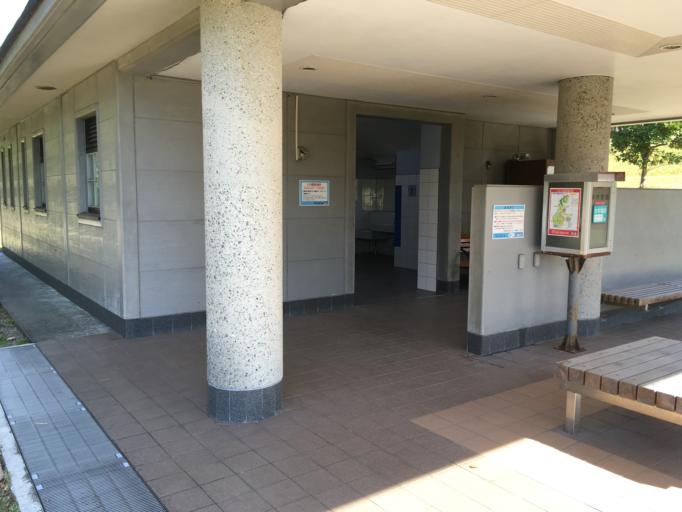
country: JP
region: Saga Prefecture
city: Kanzakimachi-kanzaki
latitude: 33.3282
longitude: 130.3858
